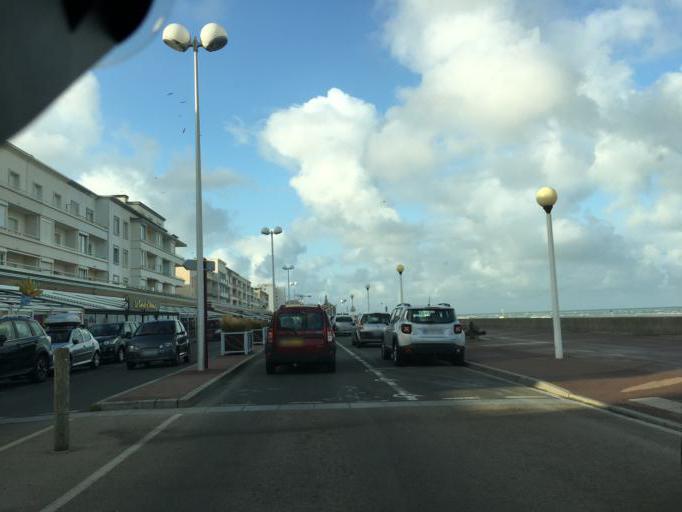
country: FR
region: Nord-Pas-de-Calais
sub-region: Departement du Pas-de-Calais
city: Berck-Plage
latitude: 50.4080
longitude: 1.5606
